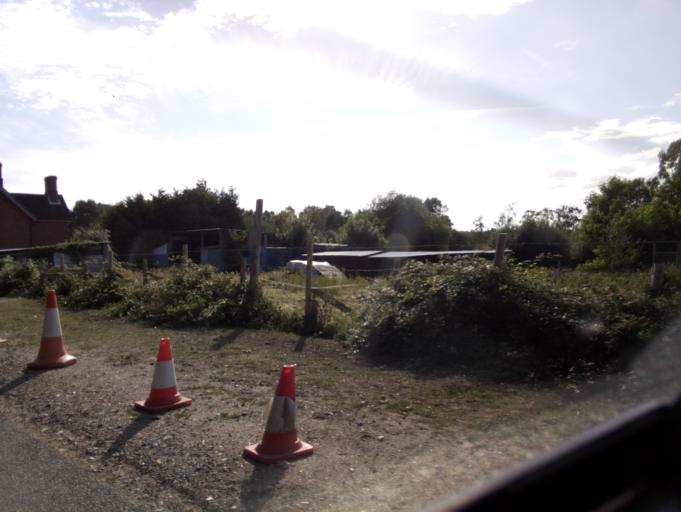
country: GB
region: England
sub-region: Hampshire
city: West Wellow
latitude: 50.9511
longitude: -1.5870
